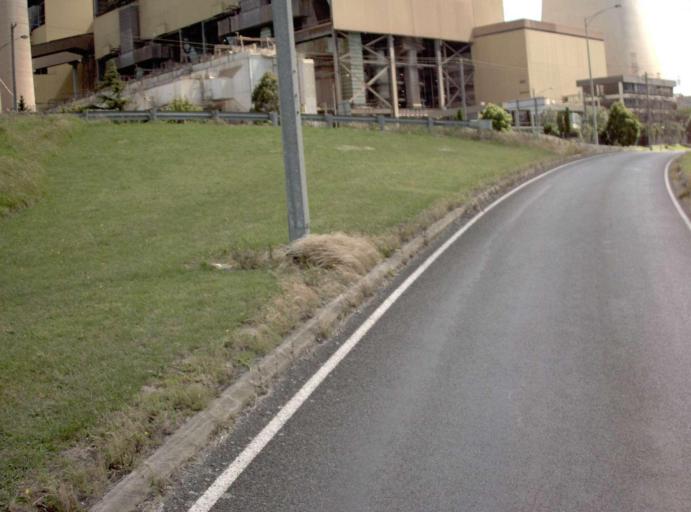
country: AU
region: Victoria
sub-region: Latrobe
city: Morwell
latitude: -38.1745
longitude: 146.3449
